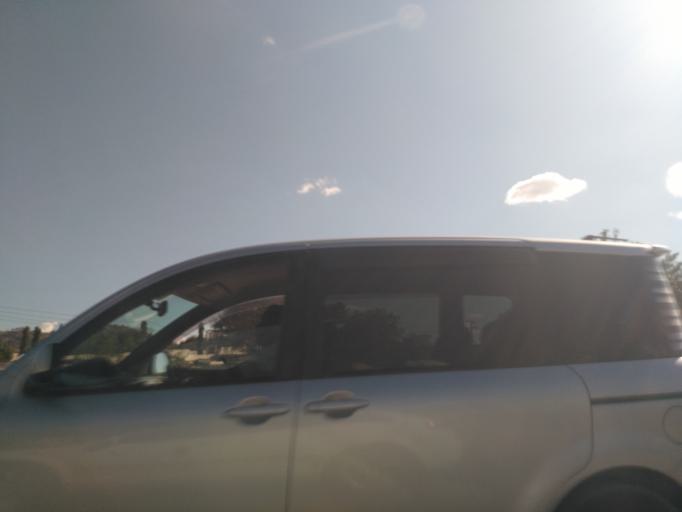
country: TZ
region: Dodoma
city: Dodoma
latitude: -6.1656
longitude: 35.7207
